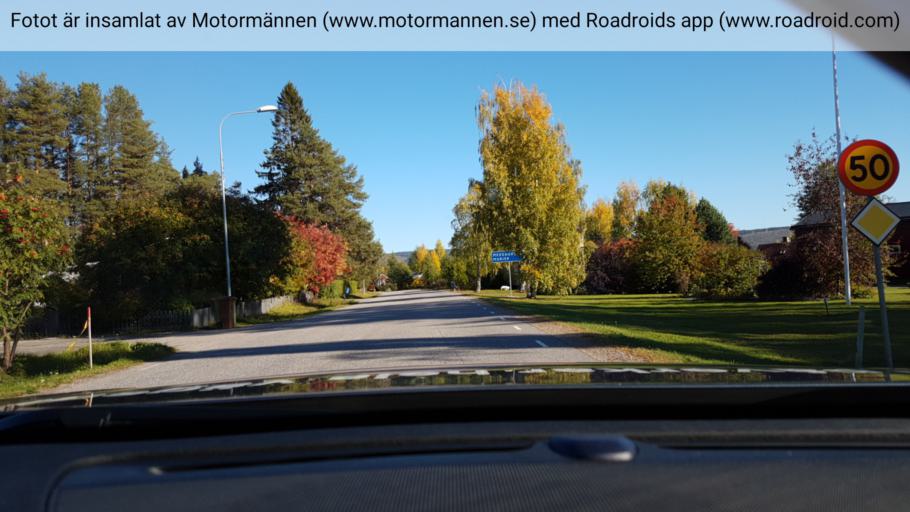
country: SE
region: Norrbotten
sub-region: Gallivare Kommun
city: Gaellivare
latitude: 66.4306
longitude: 20.6028
